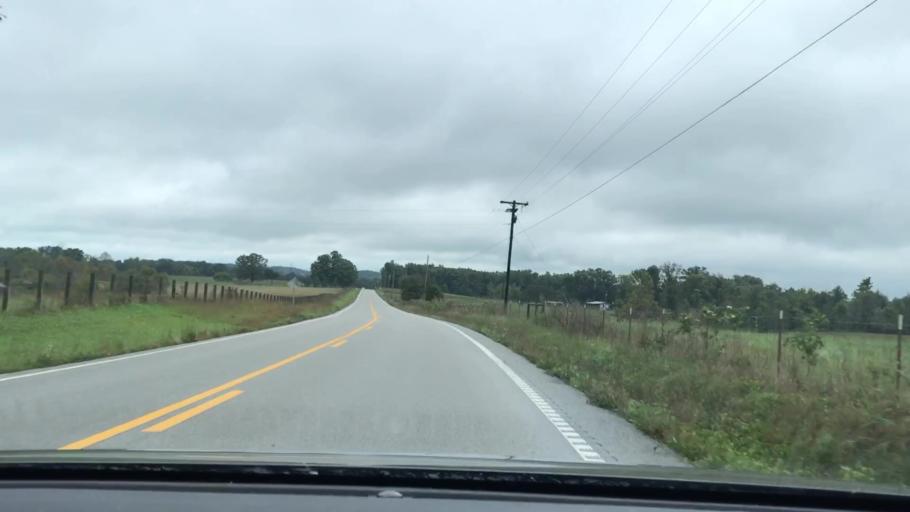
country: US
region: Tennessee
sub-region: Fentress County
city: Jamestown
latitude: 36.3648
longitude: -84.7533
